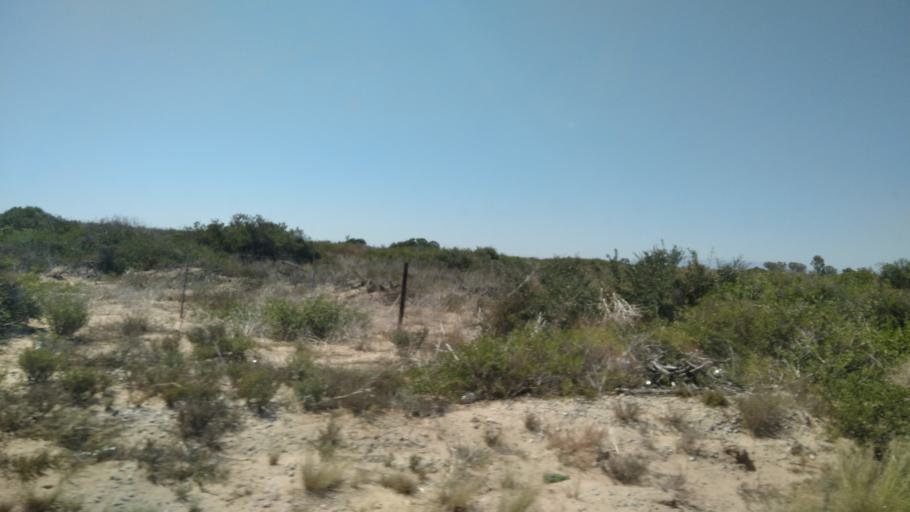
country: ZA
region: Western Cape
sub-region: West Coast District Municipality
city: Vredenburg
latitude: -32.9885
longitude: 18.1573
